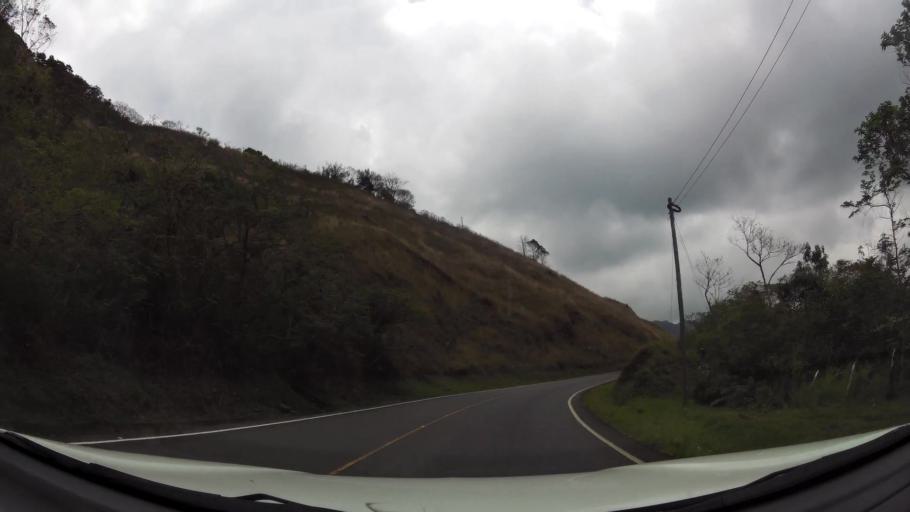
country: NI
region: Matagalpa
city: Matagalpa
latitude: 12.9904
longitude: -85.9193
